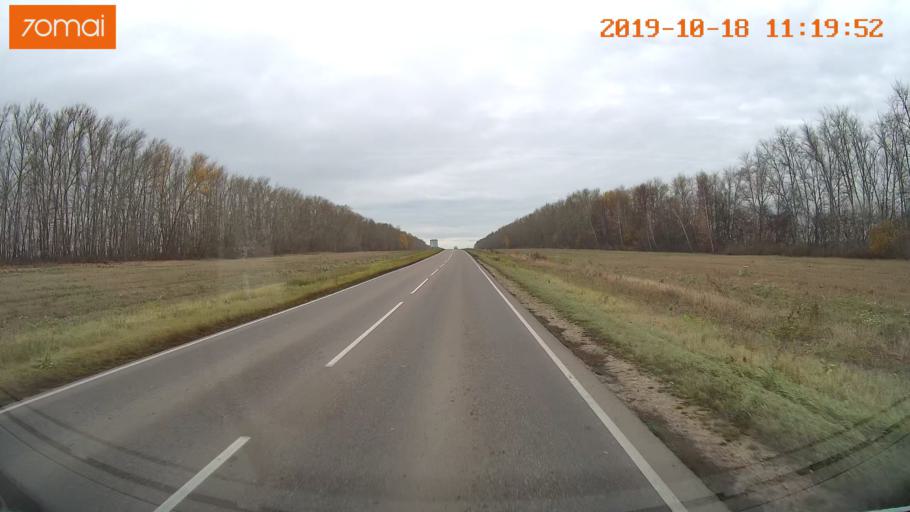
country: RU
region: Tula
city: Kimovsk
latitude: 54.0519
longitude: 38.5559
